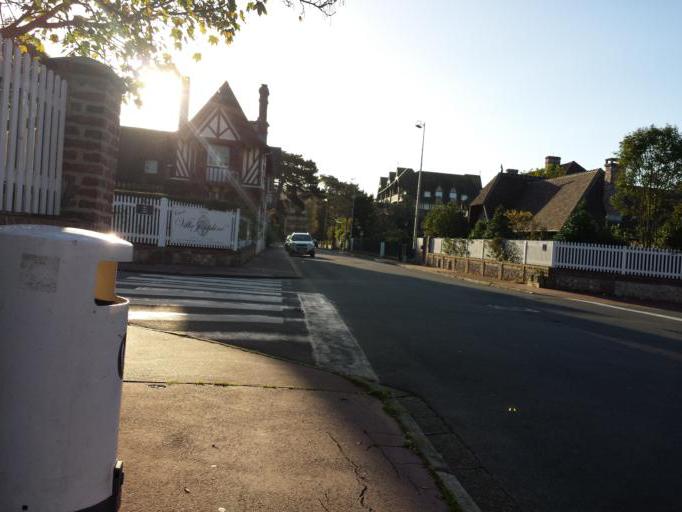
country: FR
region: Lower Normandy
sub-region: Departement du Calvados
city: Deauville
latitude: 49.3550
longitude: 0.0619
